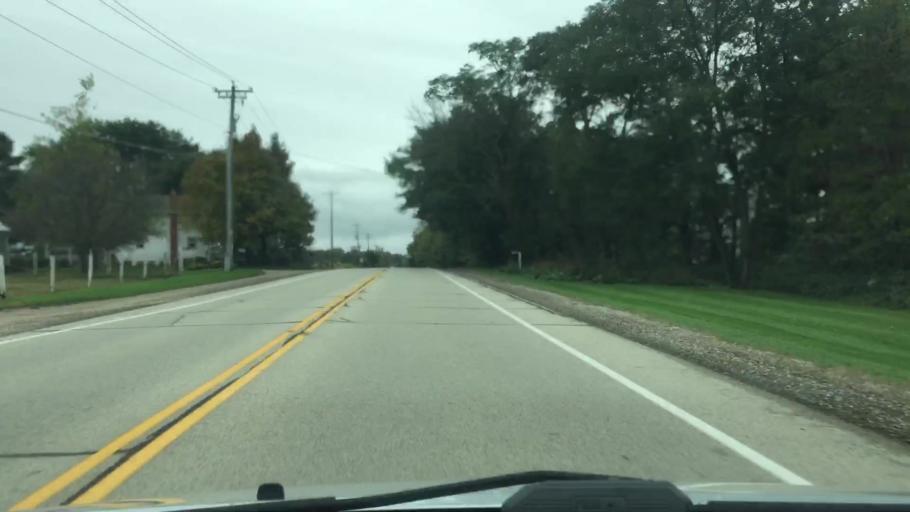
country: US
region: Wisconsin
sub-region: Walworth County
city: Elkhorn
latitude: 42.7771
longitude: -88.5545
